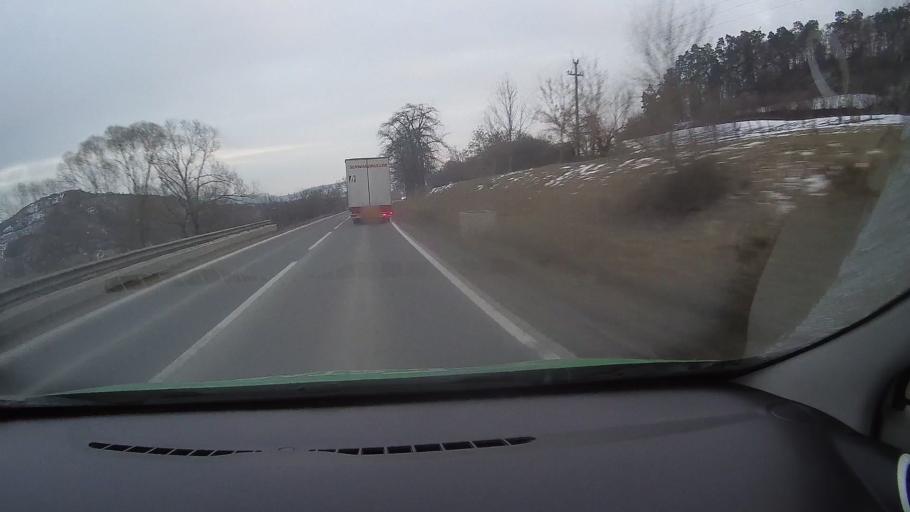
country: RO
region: Harghita
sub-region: Municipiul Odorheiu Secuiesc
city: Odorheiu Secuiesc
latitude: 46.3262
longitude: 25.2786
